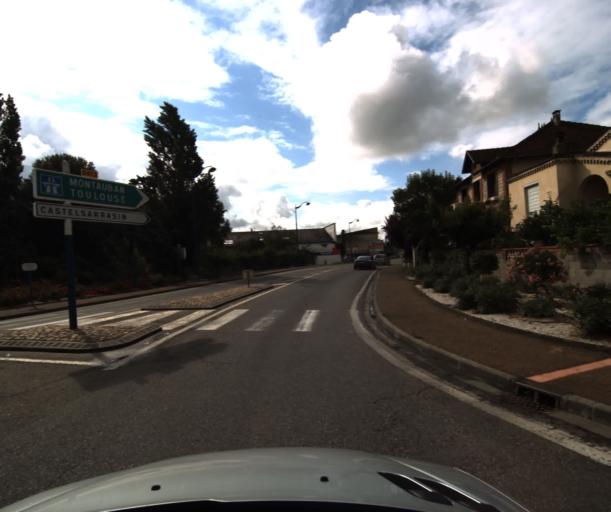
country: FR
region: Midi-Pyrenees
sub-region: Departement du Tarn-et-Garonne
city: Moissac
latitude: 44.0948
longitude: 1.0859
